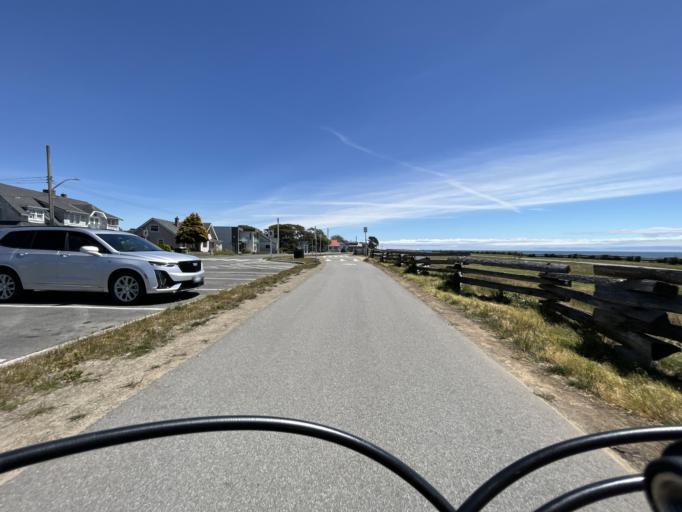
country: CA
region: British Columbia
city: Victoria
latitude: 48.4073
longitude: -123.3548
